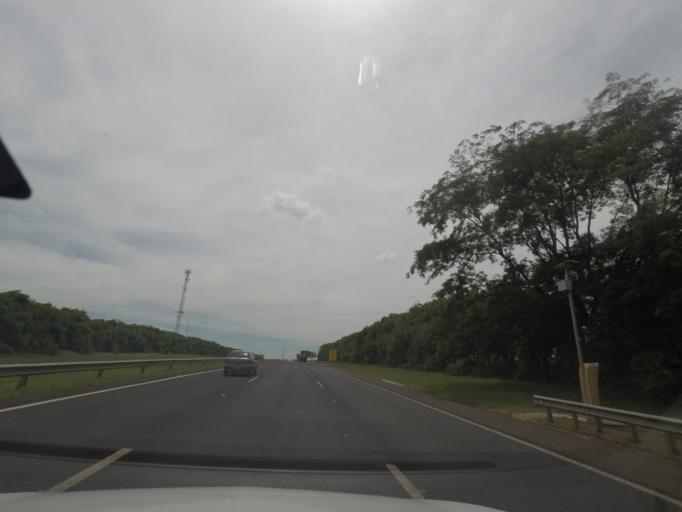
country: BR
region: Sao Paulo
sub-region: Bebedouro
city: Bebedouro
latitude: -20.9918
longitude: -48.4332
